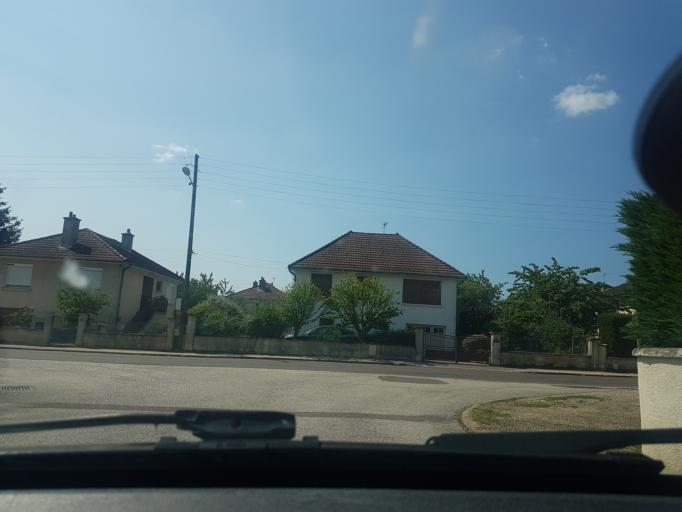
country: FR
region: Bourgogne
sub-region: Departement de Saone-et-Loire
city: Chagny
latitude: 46.9009
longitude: 4.7637
